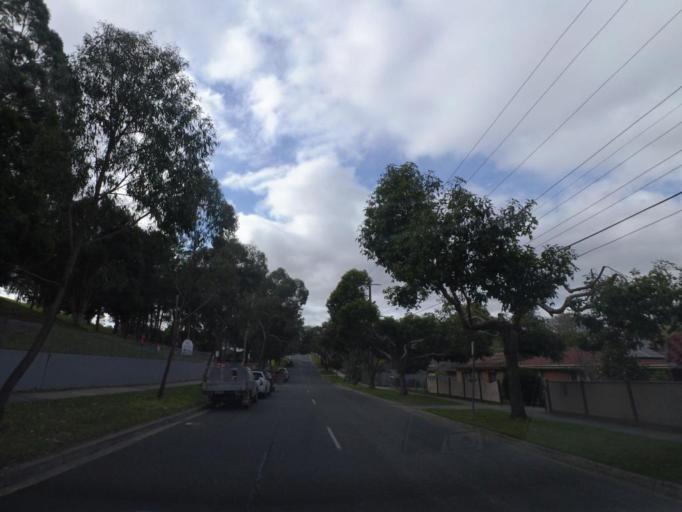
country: AU
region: Victoria
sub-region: Maroondah
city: Ringwood East
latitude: -37.8004
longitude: 145.2401
